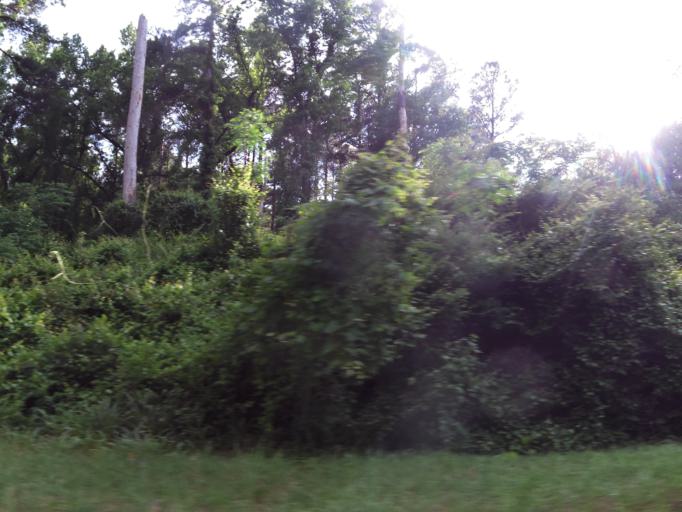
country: US
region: South Carolina
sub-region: Jasper County
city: Ridgeland
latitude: 32.5310
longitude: -81.1538
